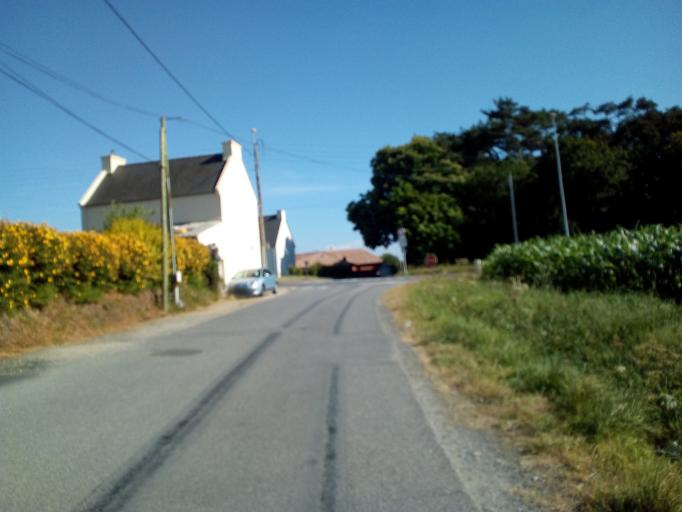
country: FR
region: Brittany
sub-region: Departement du Finistere
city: Landivisiau
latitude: 48.5090
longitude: -4.0903
